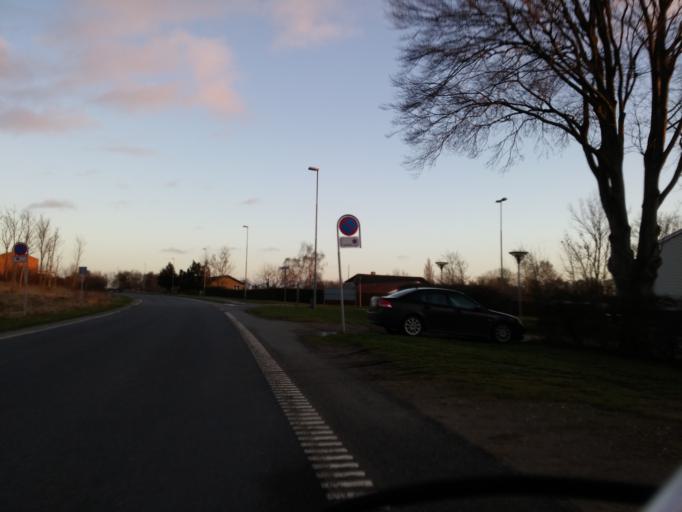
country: DK
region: South Denmark
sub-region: Kerteminde Kommune
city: Munkebo
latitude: 55.4614
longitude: 10.5494
